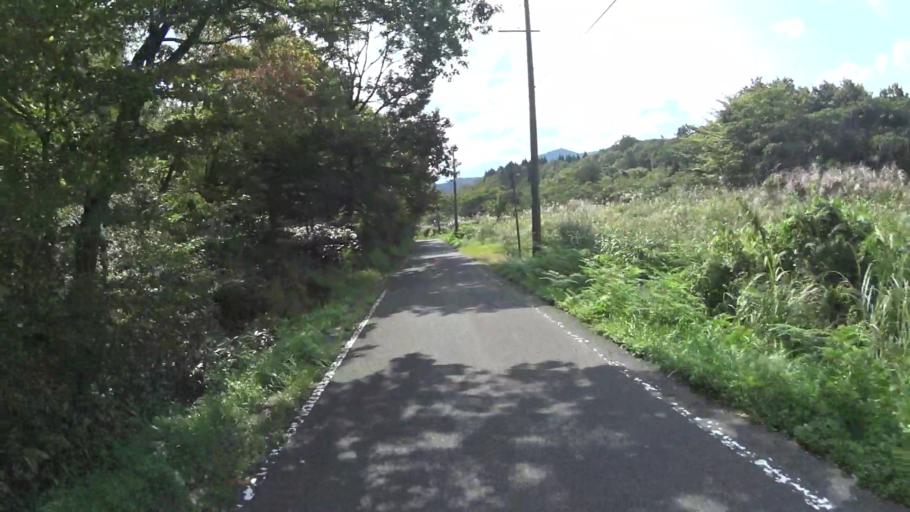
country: JP
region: Kyoto
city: Miyazu
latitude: 35.6464
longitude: 135.1806
